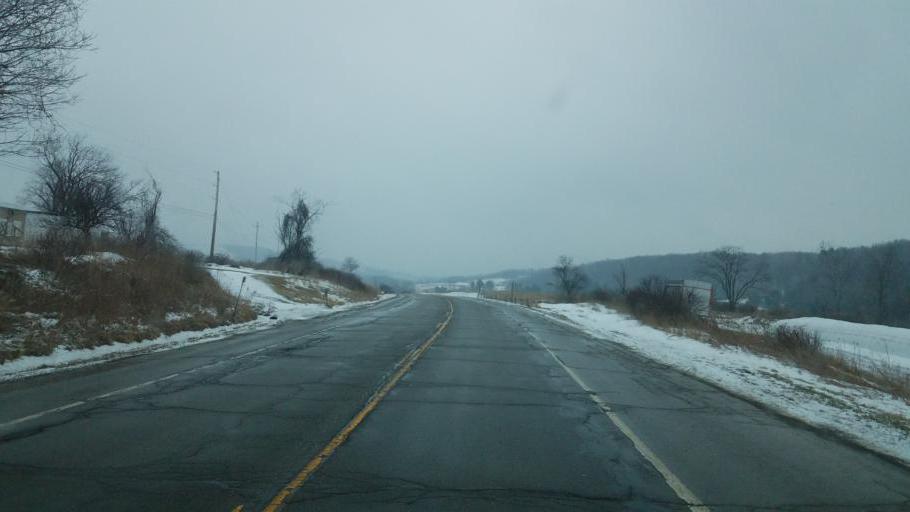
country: US
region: Pennsylvania
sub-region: Tioga County
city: Elkland
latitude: 42.0984
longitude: -77.4441
